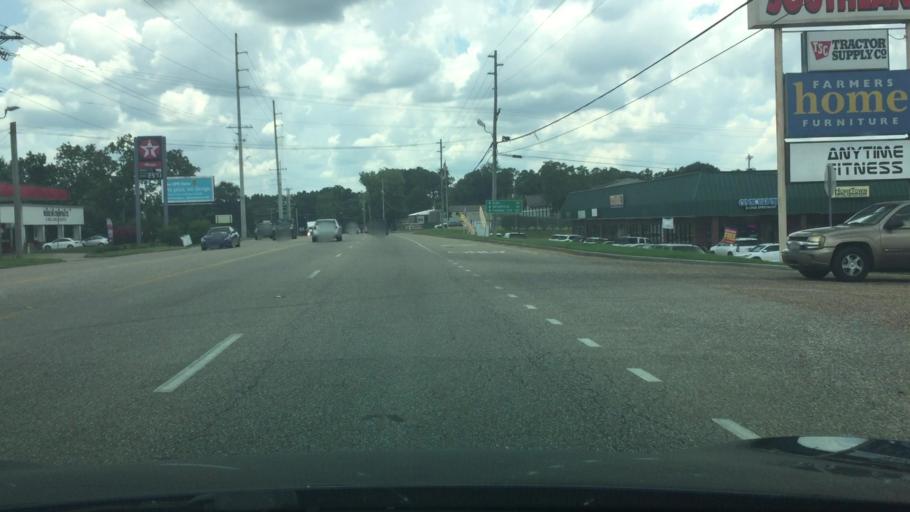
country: US
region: Alabama
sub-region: Pike County
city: Troy
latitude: 31.7844
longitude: -85.9646
